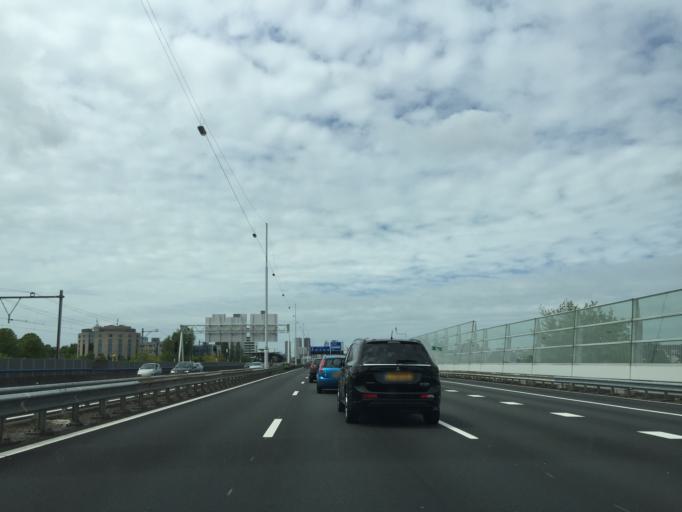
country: NL
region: South Holland
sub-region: Gemeente Leidschendam-Voorburg
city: Voorburg
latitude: 52.0651
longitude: 4.3647
